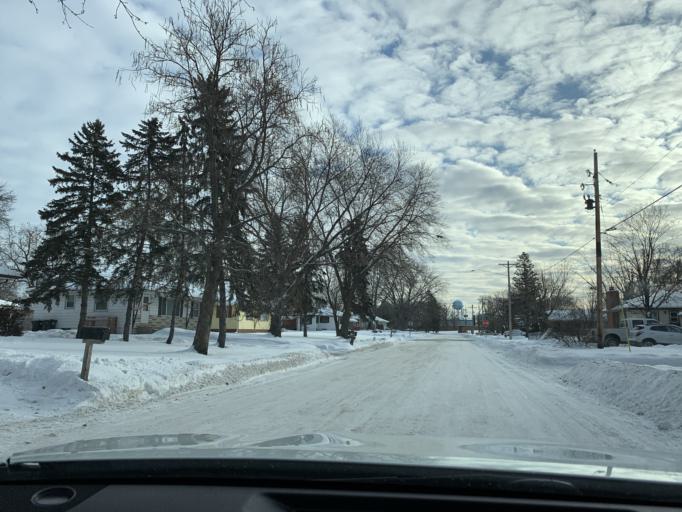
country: US
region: Minnesota
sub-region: Anoka County
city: Blaine
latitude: 45.1785
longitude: -93.2868
